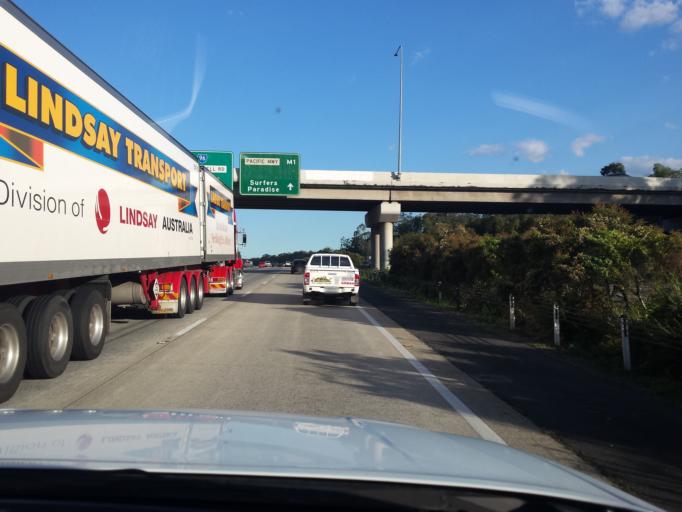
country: AU
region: Queensland
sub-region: Gold Coast
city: Ormeau Hills
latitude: -27.8055
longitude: 153.2653
